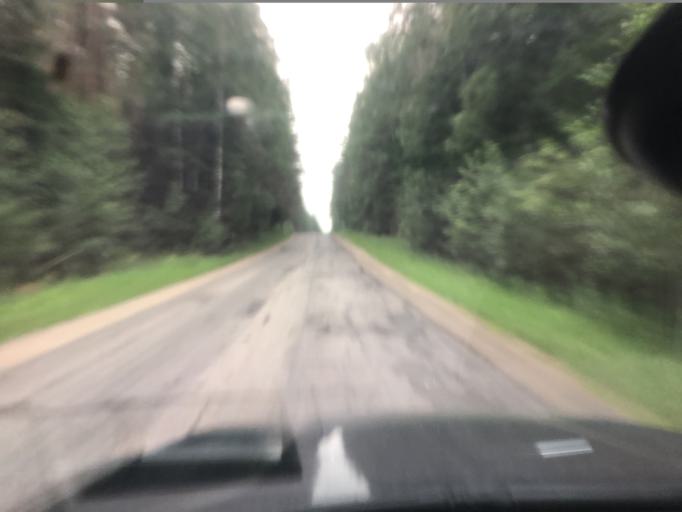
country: RU
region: Jaroslavl
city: Petrovsk
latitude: 57.0003
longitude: 39.0771
